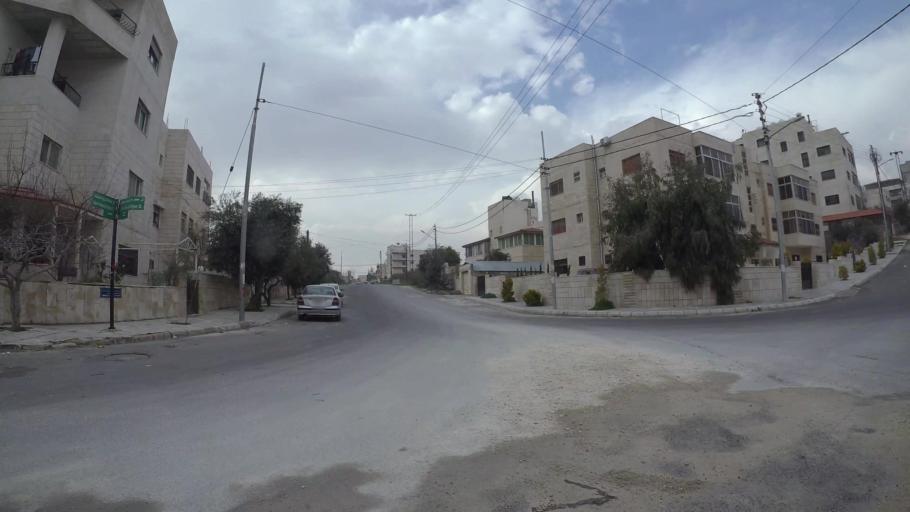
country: JO
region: Amman
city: Umm as Summaq
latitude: 31.8839
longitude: 35.8602
